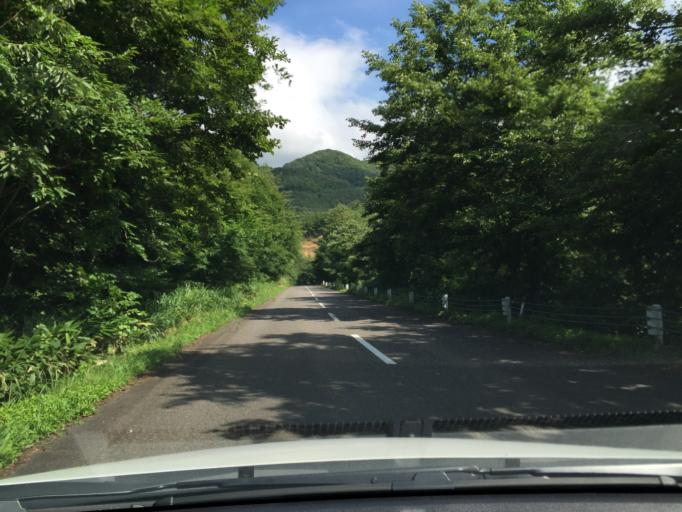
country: JP
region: Fukushima
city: Inawashiro
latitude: 37.2922
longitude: 140.0614
